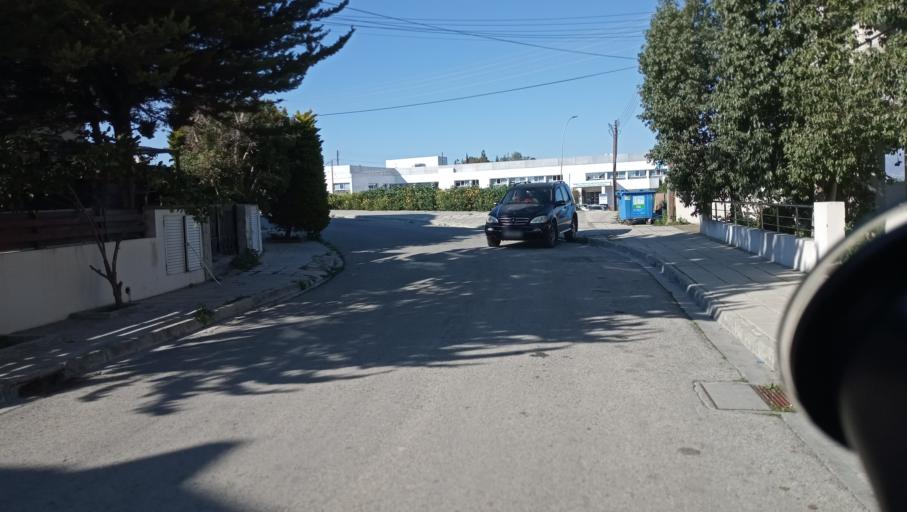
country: CY
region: Lefkosia
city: Nicosia
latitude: 35.1471
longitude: 33.3204
